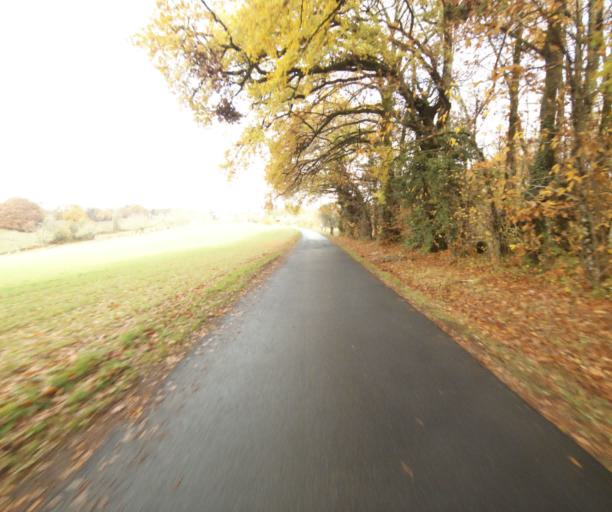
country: FR
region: Limousin
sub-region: Departement de la Correze
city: Saint-Mexant
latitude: 45.2356
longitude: 1.6342
